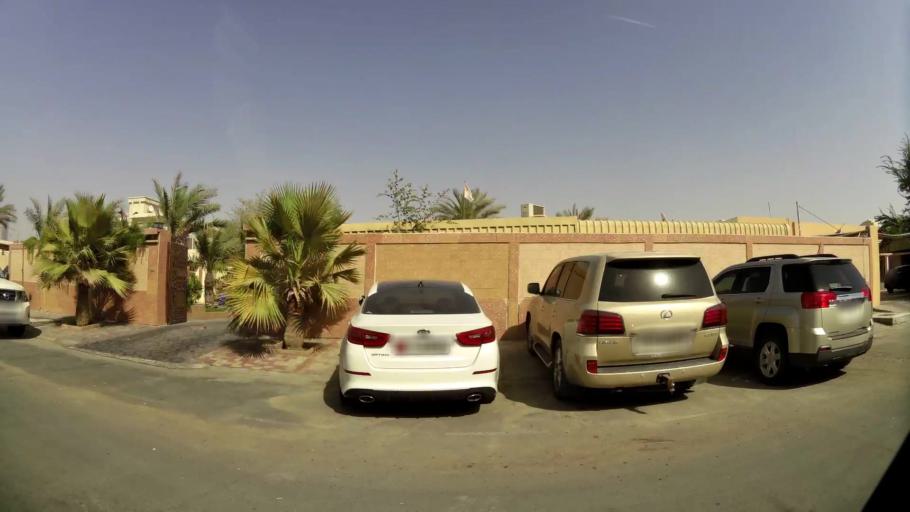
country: AE
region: Dubai
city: Dubai
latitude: 25.1759
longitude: 55.2495
